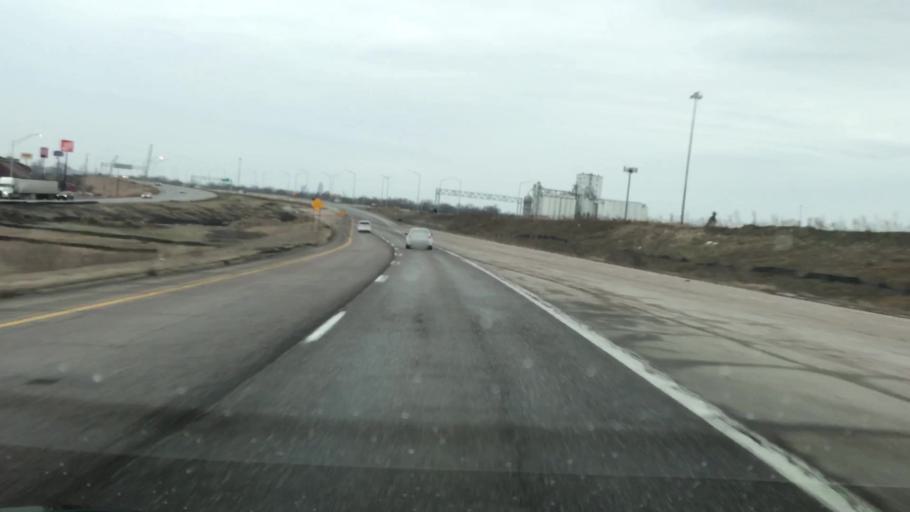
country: US
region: Iowa
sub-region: Pottawattamie County
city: Council Bluffs
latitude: 41.2313
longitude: -95.8428
